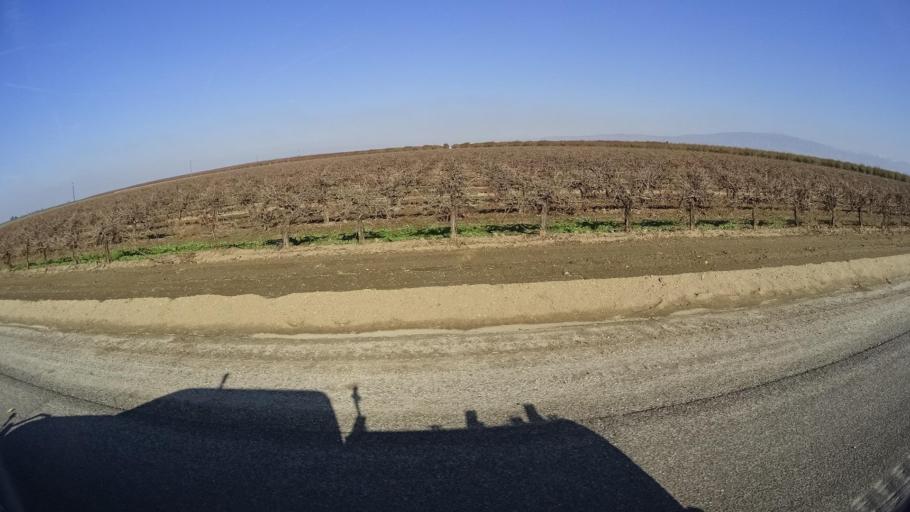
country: US
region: California
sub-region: Kern County
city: Arvin
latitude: 35.2089
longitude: -118.8676
